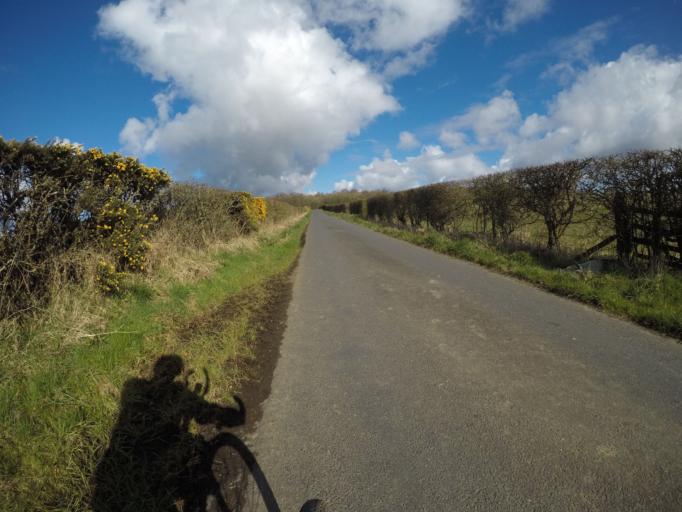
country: GB
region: Scotland
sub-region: North Ayrshire
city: Irvine
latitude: 55.6696
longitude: -4.6522
